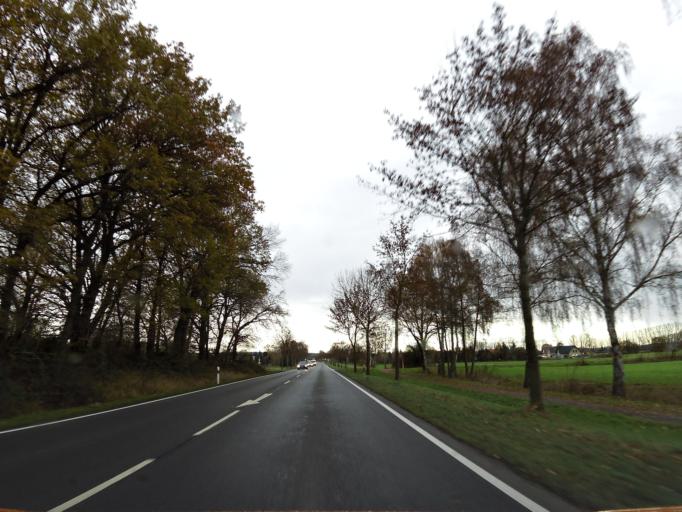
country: DE
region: Saxony-Anhalt
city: Gardelegen
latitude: 52.5397
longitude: 11.3712
